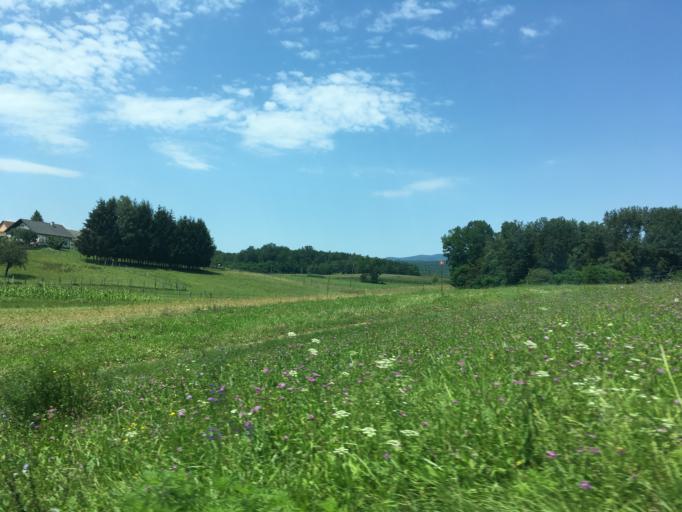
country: SI
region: Metlika
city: Metlika
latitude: 45.6492
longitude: 15.3550
